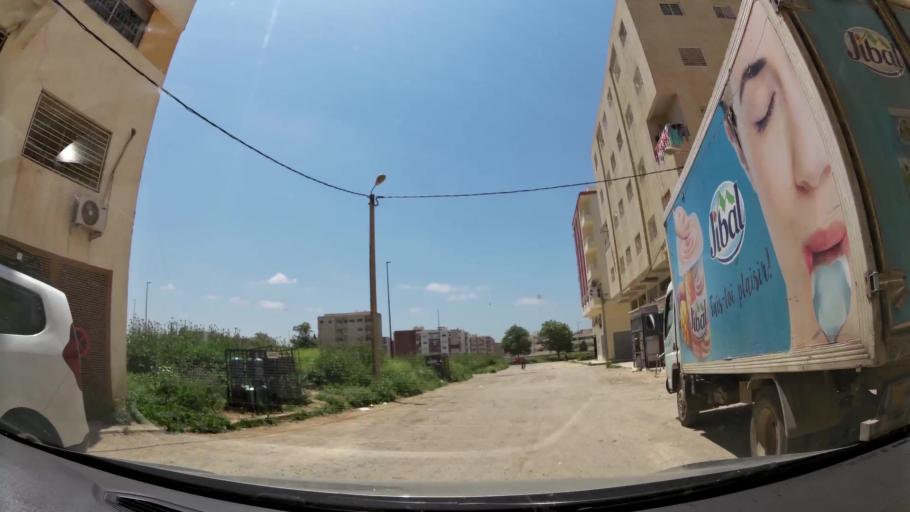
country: MA
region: Fes-Boulemane
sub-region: Fes
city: Fes
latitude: 34.0302
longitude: -5.0416
